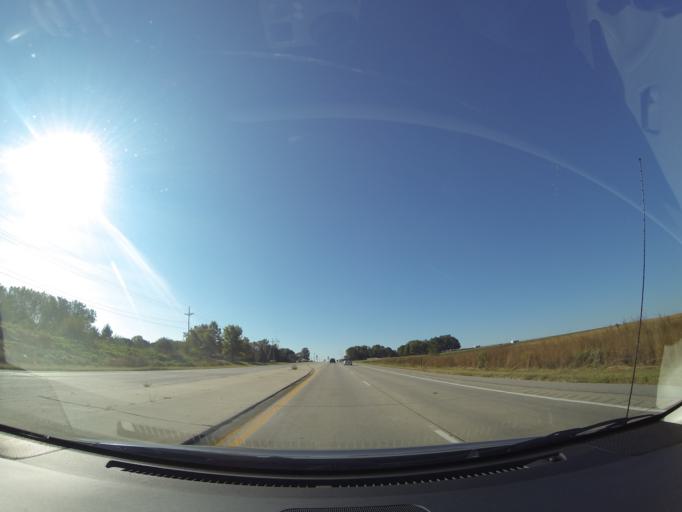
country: US
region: Nebraska
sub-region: Sarpy County
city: Gretna
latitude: 41.1657
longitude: -96.2343
